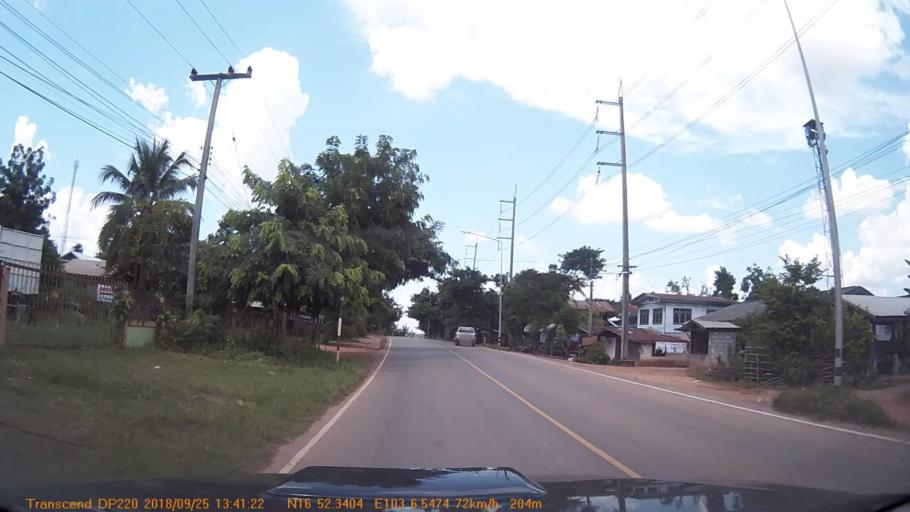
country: TH
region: Changwat Udon Thani
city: Si That
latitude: 16.8723
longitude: 103.1091
